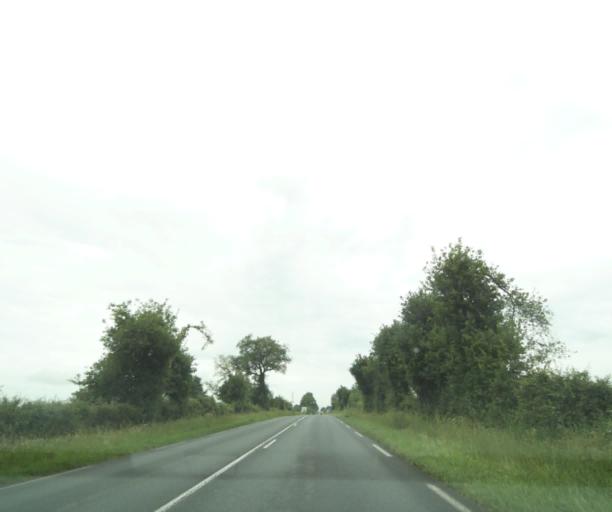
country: FR
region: Poitou-Charentes
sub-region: Departement des Deux-Sevres
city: Viennay
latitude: 46.7167
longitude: -0.2390
